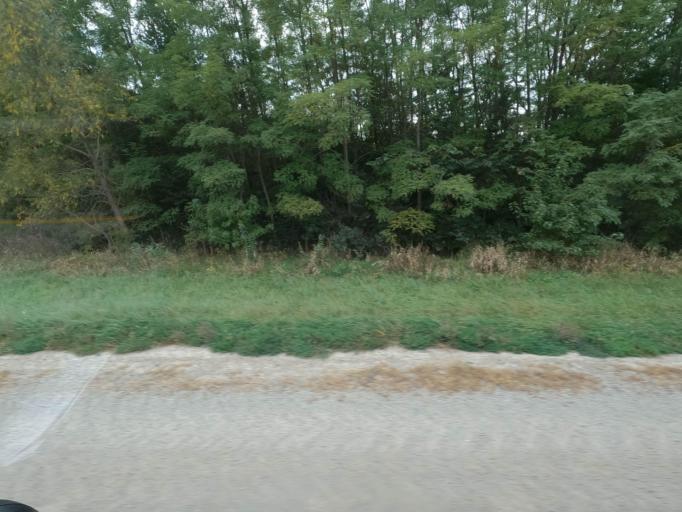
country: US
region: Iowa
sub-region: Marion County
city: Pella
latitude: 41.3991
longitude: -92.9351
